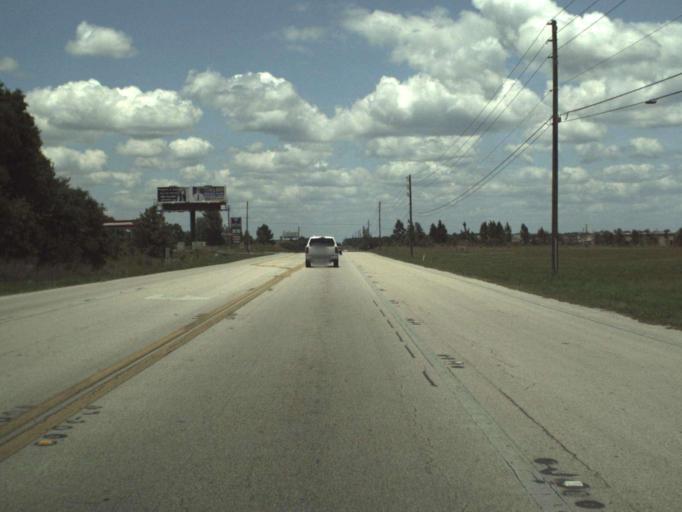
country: US
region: Florida
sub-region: Marion County
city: Silver Springs Shores
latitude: 29.1024
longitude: -82.0535
